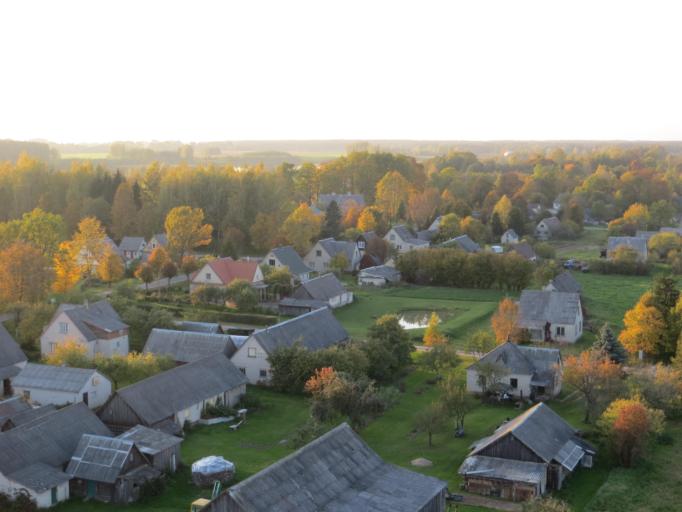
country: LT
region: Panevezys
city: Rokiskis
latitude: 55.7403
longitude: 25.5304
